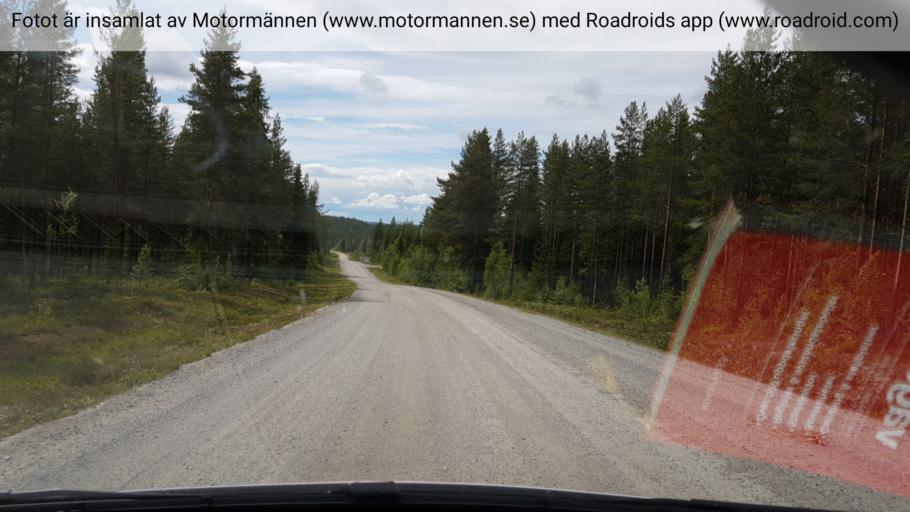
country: SE
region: Vaesternorrland
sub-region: Solleftea Kommun
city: Solleftea
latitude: 63.3240
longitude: 17.3482
